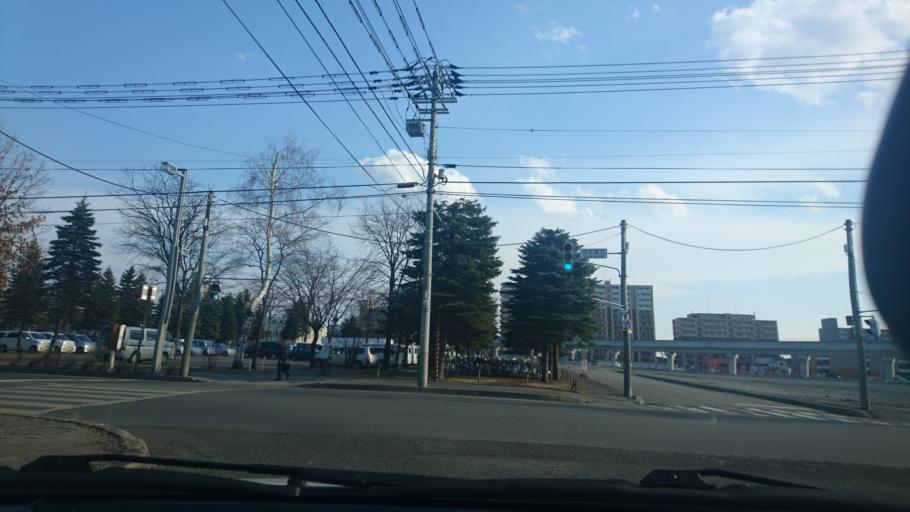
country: JP
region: Hokkaido
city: Obihiro
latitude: 42.9234
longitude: 143.1956
